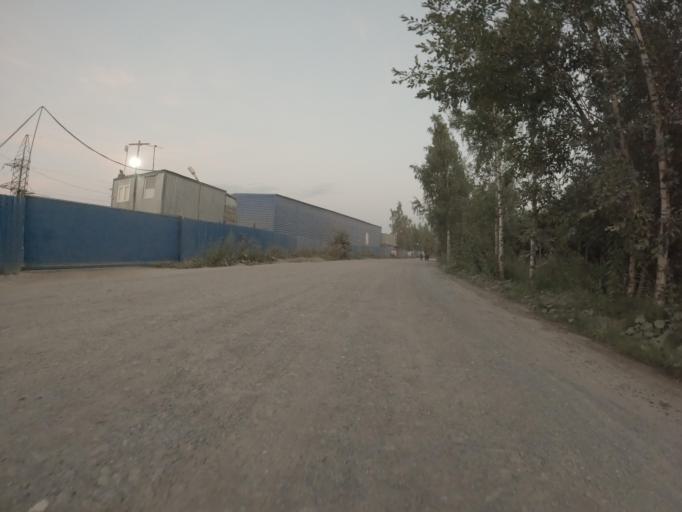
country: RU
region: Leningrad
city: Yanino Vtoroye
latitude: 59.9401
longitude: 30.6013
